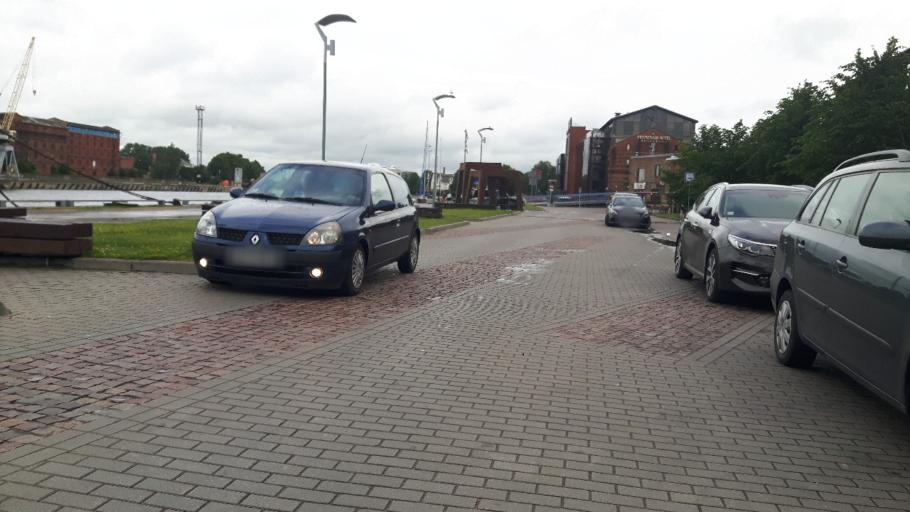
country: LV
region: Liepaja
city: Liepaja
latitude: 56.5130
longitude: 21.0090
